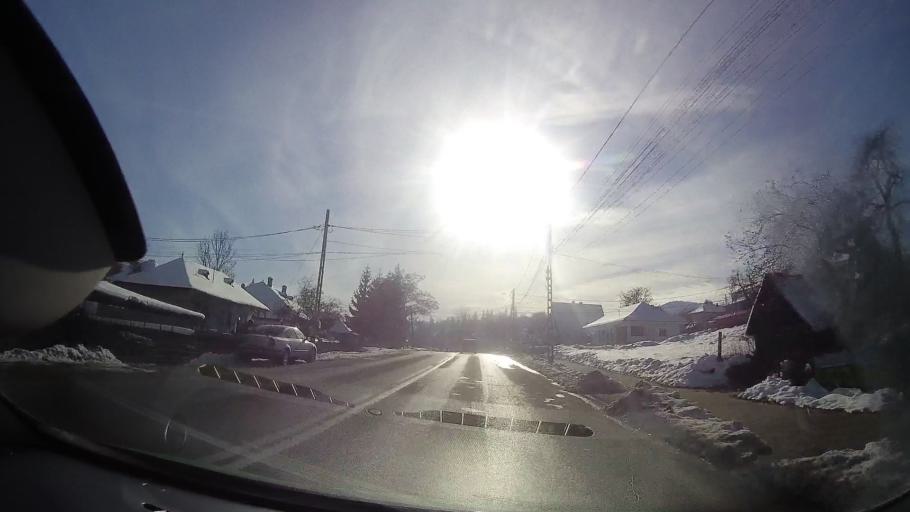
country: RO
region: Neamt
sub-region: Comuna Baltatesti
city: Baltatesti
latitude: 47.1240
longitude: 26.3103
